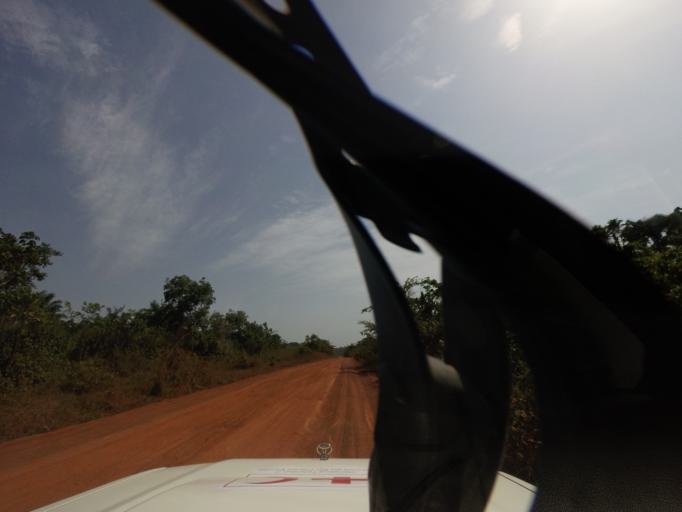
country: LR
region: Bong
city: Gbarnga
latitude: 7.0555
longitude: -9.4669
